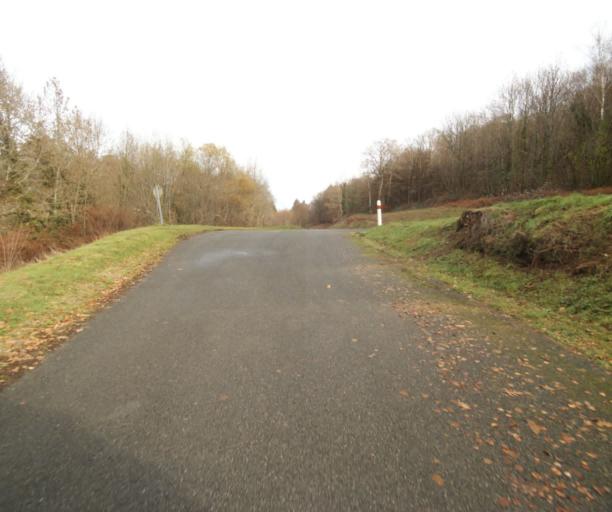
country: FR
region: Limousin
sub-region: Departement de la Correze
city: Chameyrat
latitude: 45.2611
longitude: 1.6802
